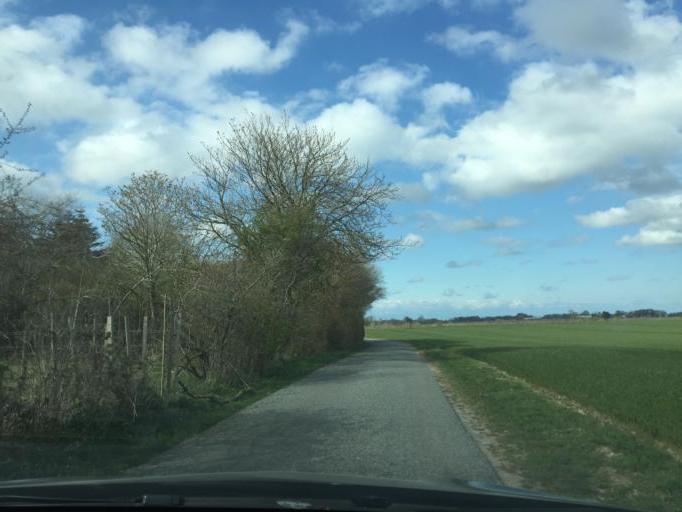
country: DK
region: South Denmark
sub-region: Faaborg-Midtfyn Kommune
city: Arslev
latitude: 55.3217
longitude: 10.4637
